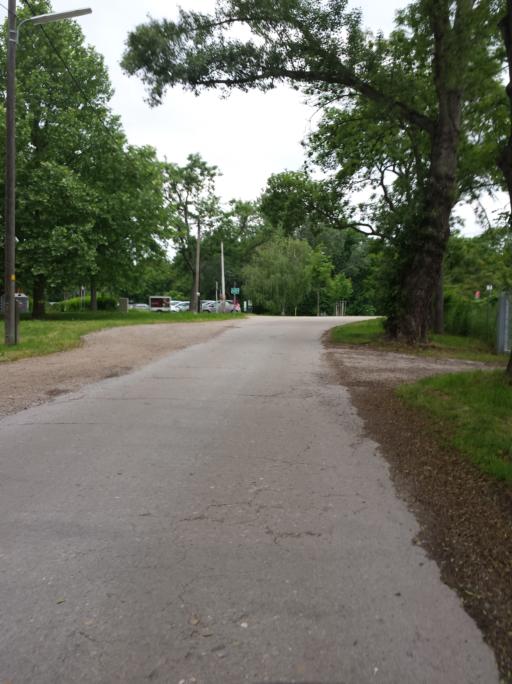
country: AT
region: Lower Austria
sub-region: Politischer Bezirk Wien-Umgebung
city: Schwechat
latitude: 48.1880
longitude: 16.4368
